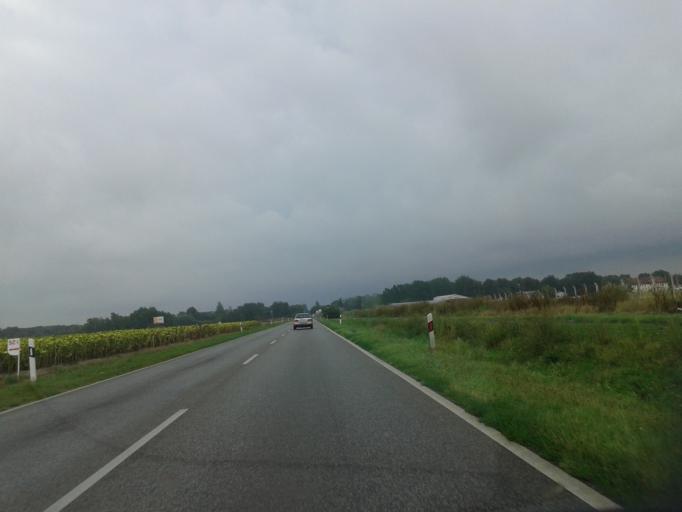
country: HU
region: Csongrad
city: Szeged
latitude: 46.2531
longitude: 20.0911
